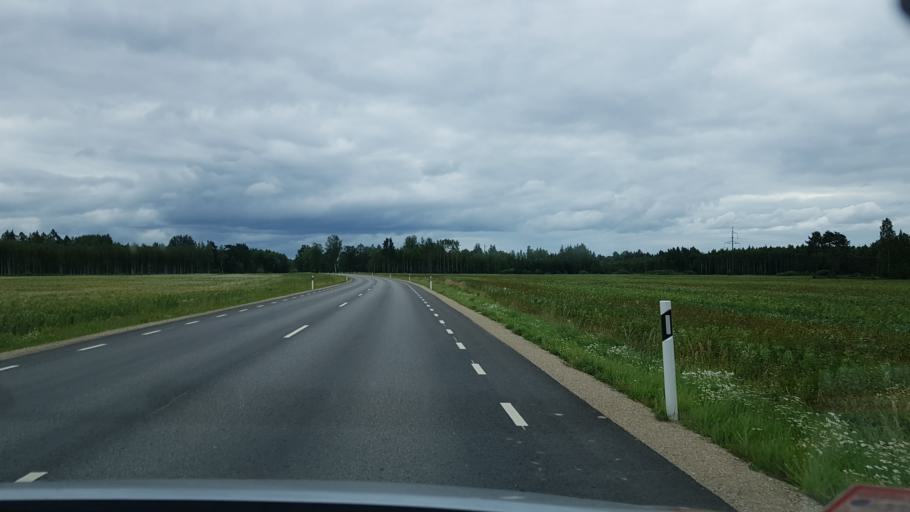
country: EE
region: Polvamaa
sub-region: Polva linn
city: Polva
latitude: 58.0800
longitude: 27.2413
